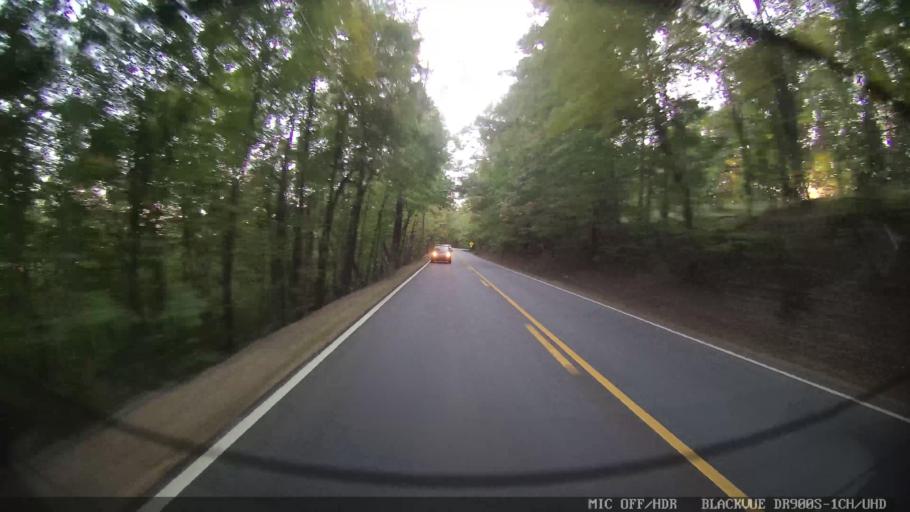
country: US
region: Georgia
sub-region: Lumpkin County
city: Dahlonega
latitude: 34.6195
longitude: -83.9589
